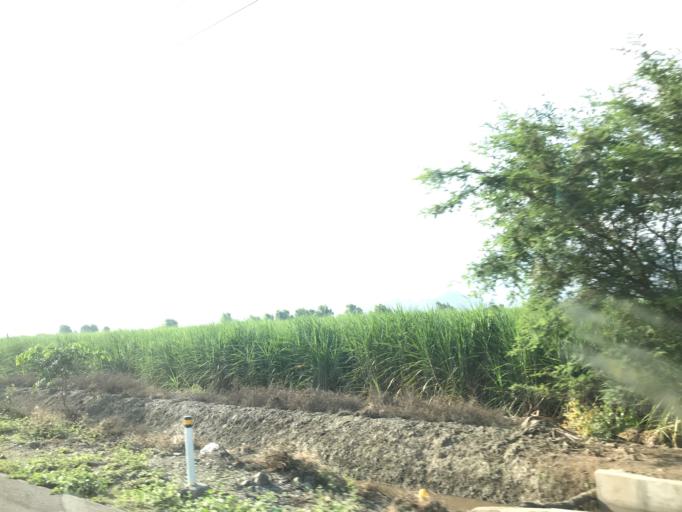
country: PE
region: Lambayeque
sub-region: Provincia de Chiclayo
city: Chongoyape
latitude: -6.6761
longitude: -79.4419
